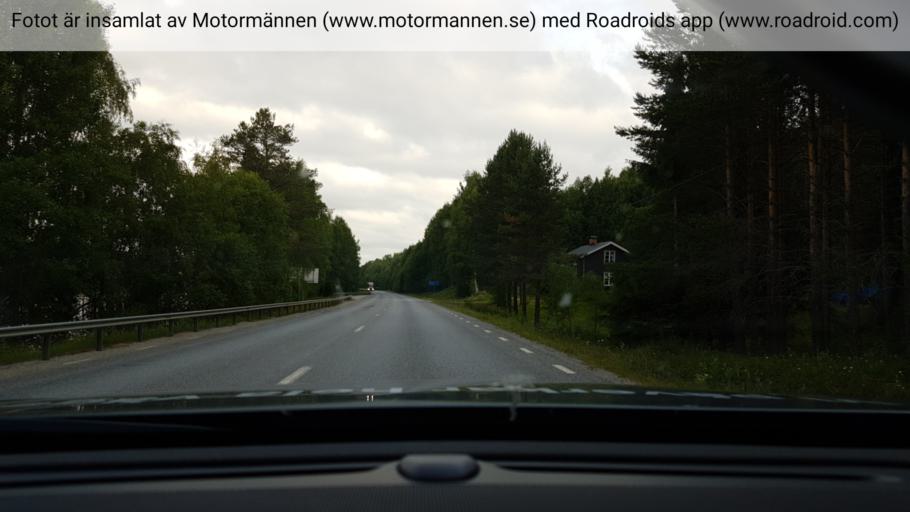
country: SE
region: Vaesterbotten
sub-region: Vindelns Kommun
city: Vindeln
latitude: 64.2956
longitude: 19.6195
